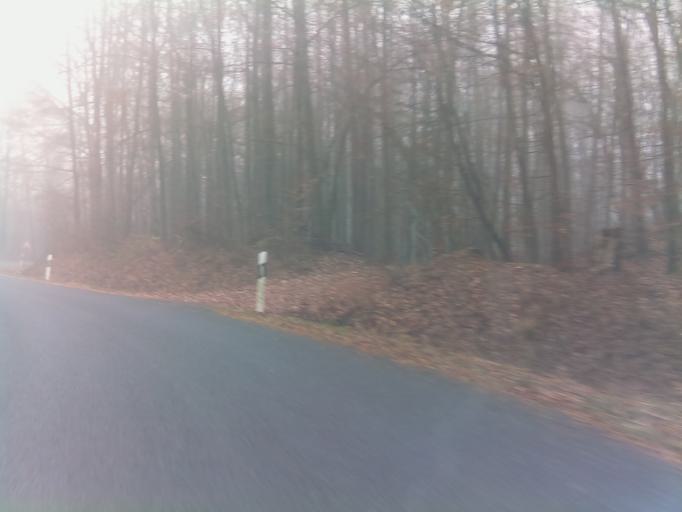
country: DE
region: Bavaria
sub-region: Regierungsbezirk Unterfranken
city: Hofheim in Unterfranken
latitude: 50.0921
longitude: 10.5853
